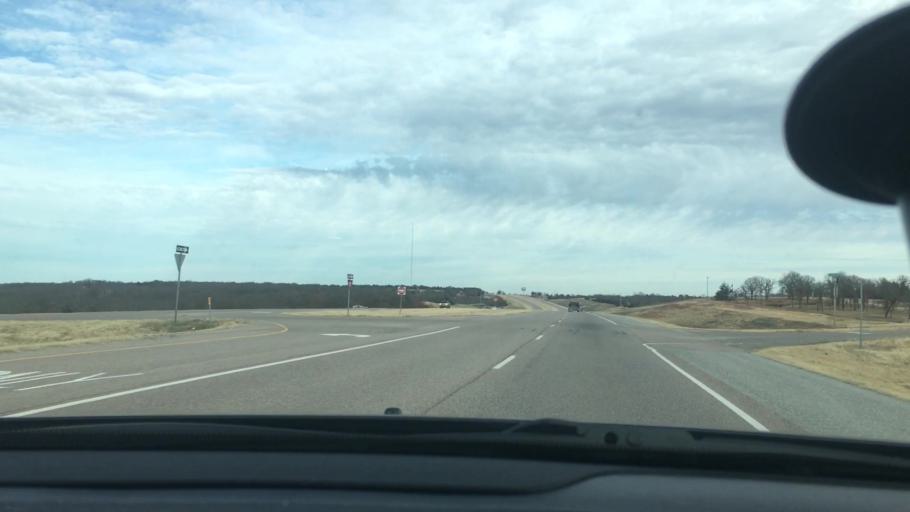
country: US
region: Oklahoma
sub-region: Pontotoc County
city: Byng
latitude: 34.8754
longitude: -96.6774
